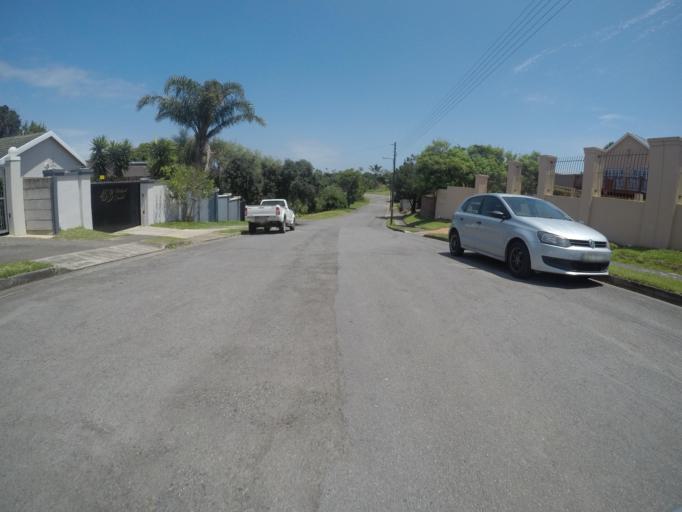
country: ZA
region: Eastern Cape
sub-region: Buffalo City Metropolitan Municipality
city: East London
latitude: -33.0028
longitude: 27.9185
